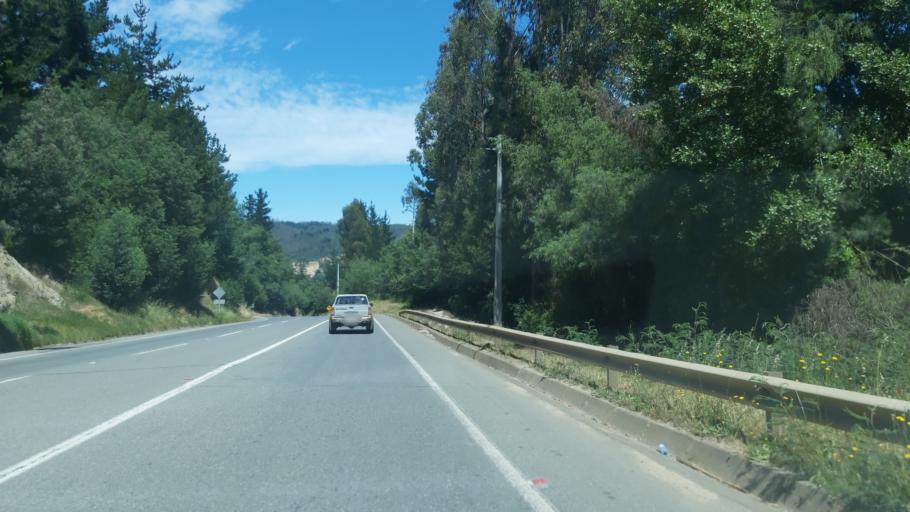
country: CL
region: Maule
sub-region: Provincia de Talca
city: Constitucion
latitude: -35.3319
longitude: -72.3874
